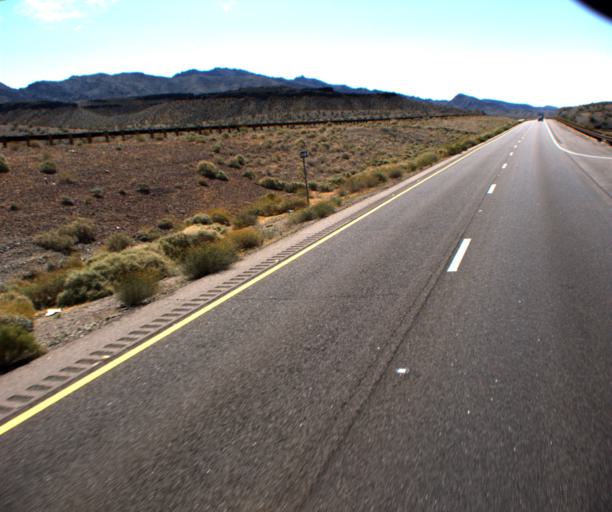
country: US
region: Nevada
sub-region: Clark County
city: Boulder City
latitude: 35.9454
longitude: -114.6448
